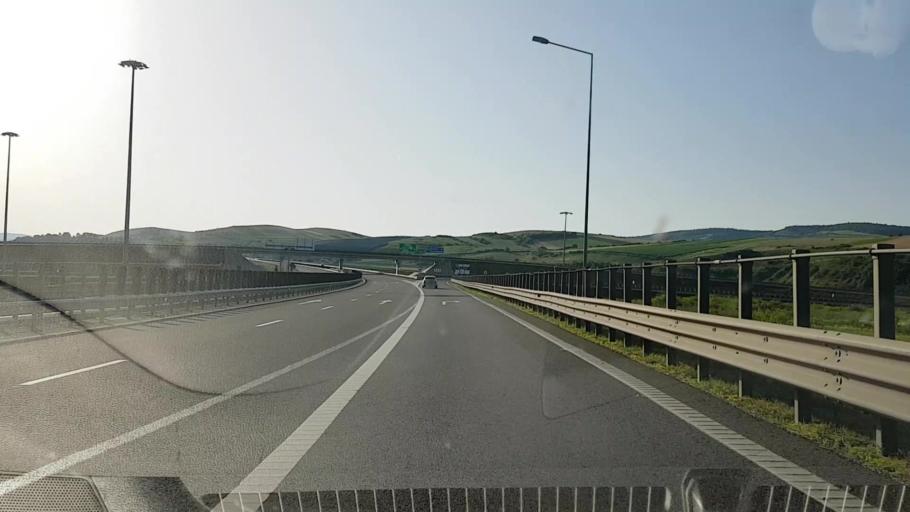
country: RO
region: Cluj
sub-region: Comuna Floresti
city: Luna de Sus
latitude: 46.7540
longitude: 23.4133
